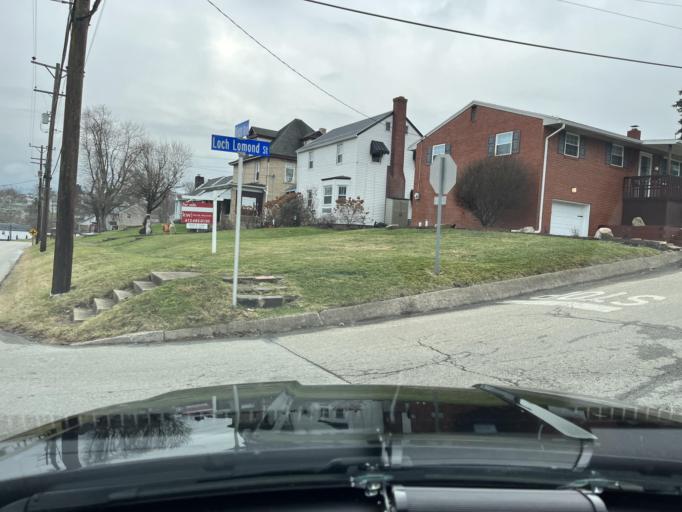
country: US
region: Pennsylvania
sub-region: Fayette County
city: South Uniontown
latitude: 39.8949
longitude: -79.7432
